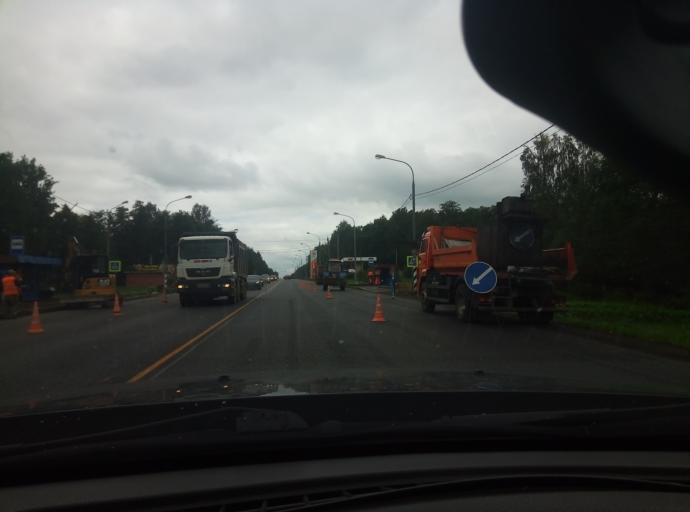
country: RU
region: Kaluga
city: Belousovo
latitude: 55.0875
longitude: 36.6524
